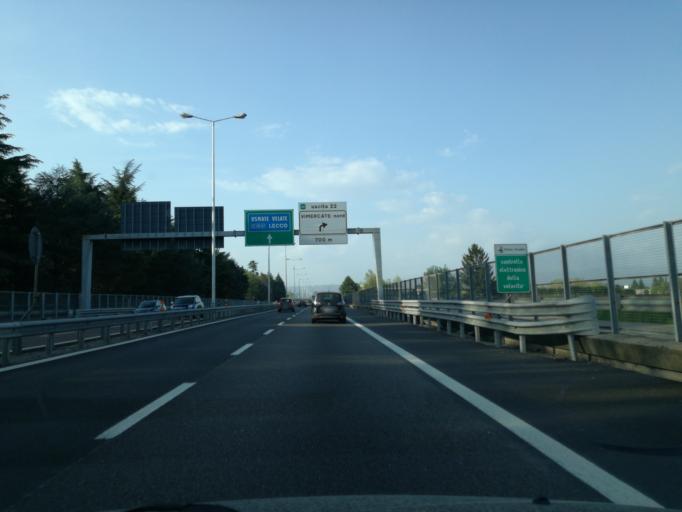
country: IT
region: Lombardy
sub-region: Provincia di Monza e Brianza
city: Velasca
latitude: 45.6274
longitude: 9.3619
